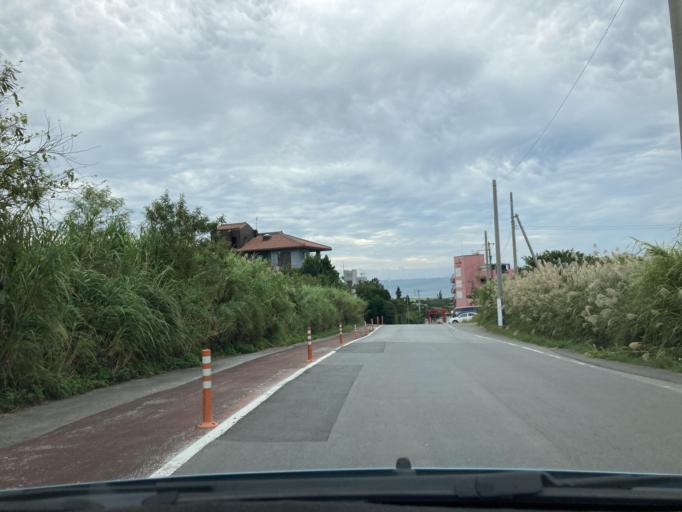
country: JP
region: Okinawa
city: Okinawa
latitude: 26.3869
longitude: 127.7403
